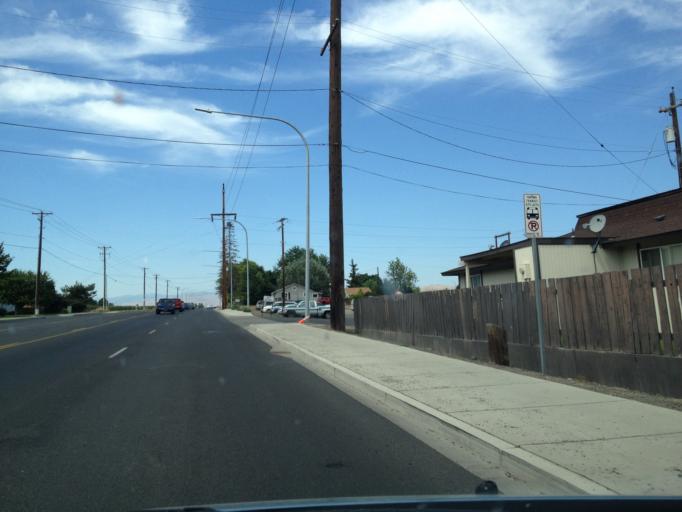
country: US
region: Washington
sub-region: Yakima County
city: West Valley
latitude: 46.5855
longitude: -120.5756
